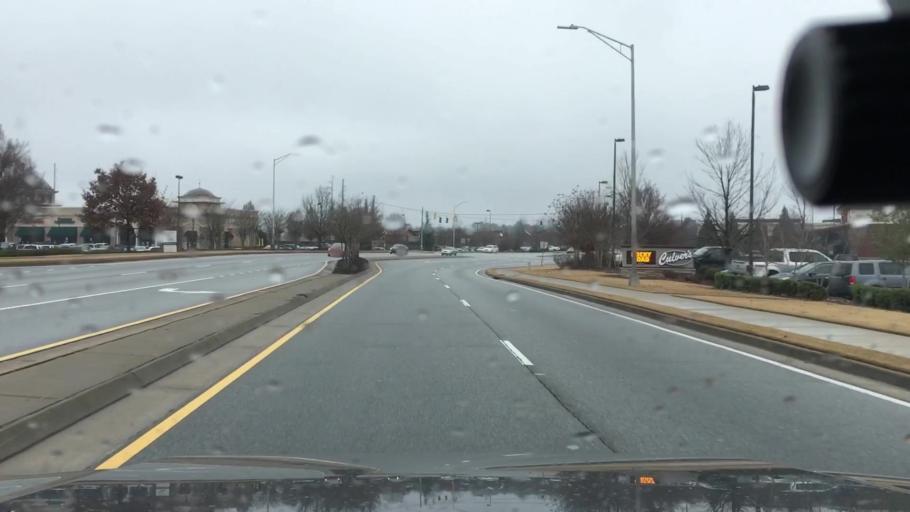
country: US
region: Georgia
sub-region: Coweta County
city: Newnan
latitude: 33.3900
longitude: -84.7625
